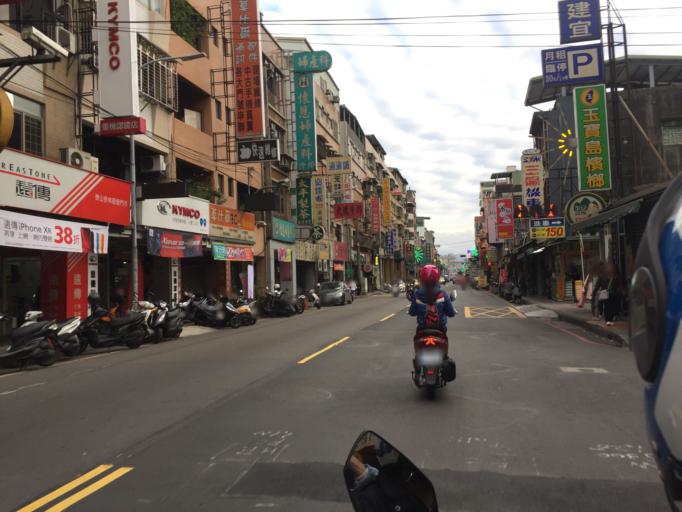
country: TW
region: Taipei
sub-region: Taipei
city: Banqiao
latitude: 25.0609
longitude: 121.4336
